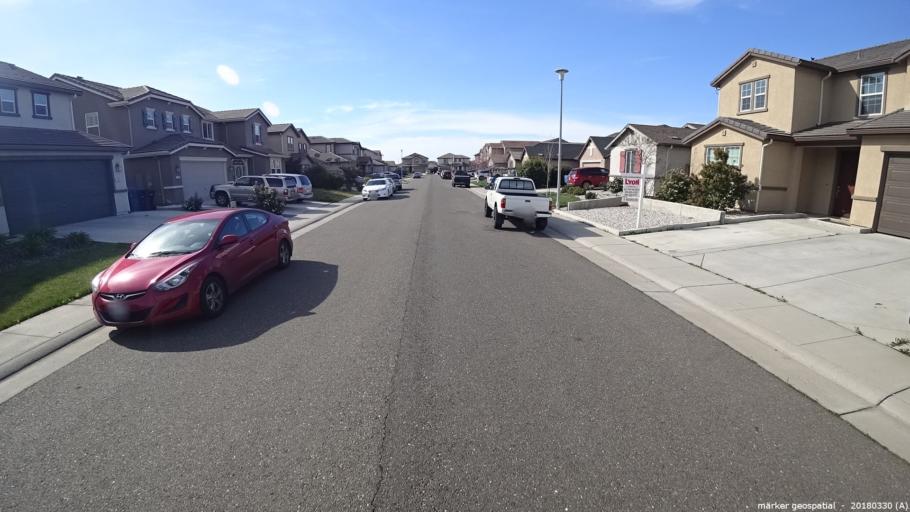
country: US
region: California
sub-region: Sacramento County
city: Vineyard
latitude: 38.4863
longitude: -121.3449
